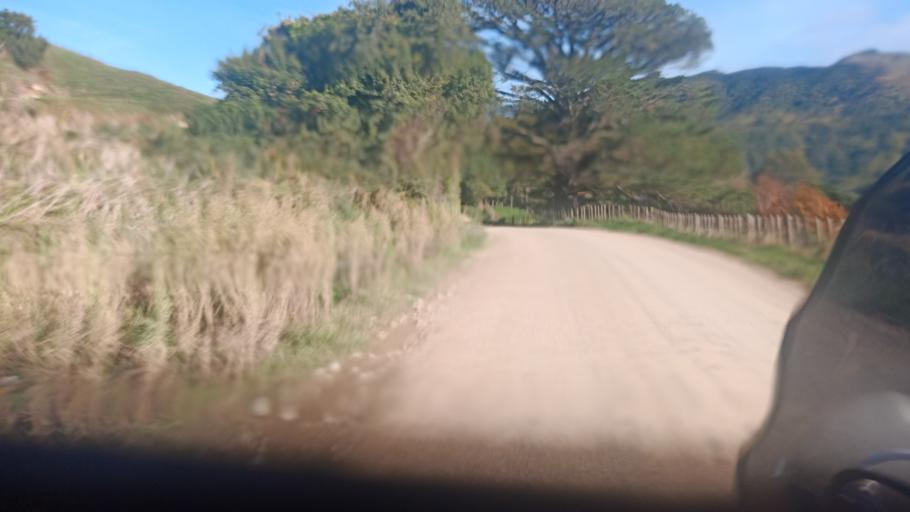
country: NZ
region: Bay of Plenty
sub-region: Opotiki District
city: Opotiki
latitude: -38.4340
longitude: 177.5525
